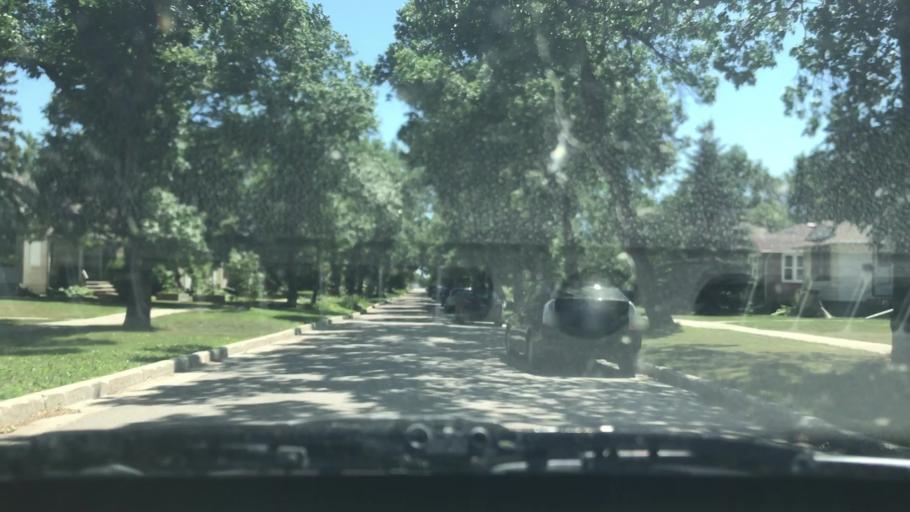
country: CA
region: Manitoba
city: Winnipeg
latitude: 49.8708
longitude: -97.1959
